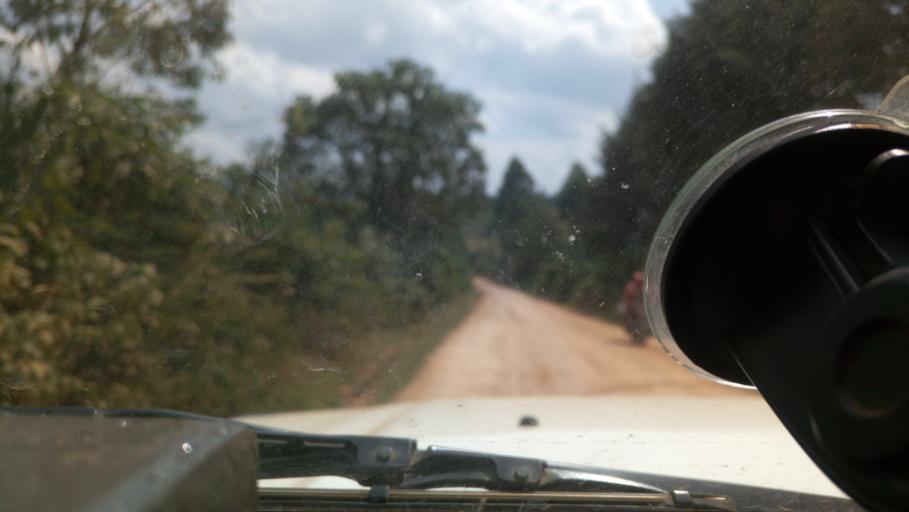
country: KE
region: Kericho
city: Sotik
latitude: -0.5932
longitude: 35.0898
